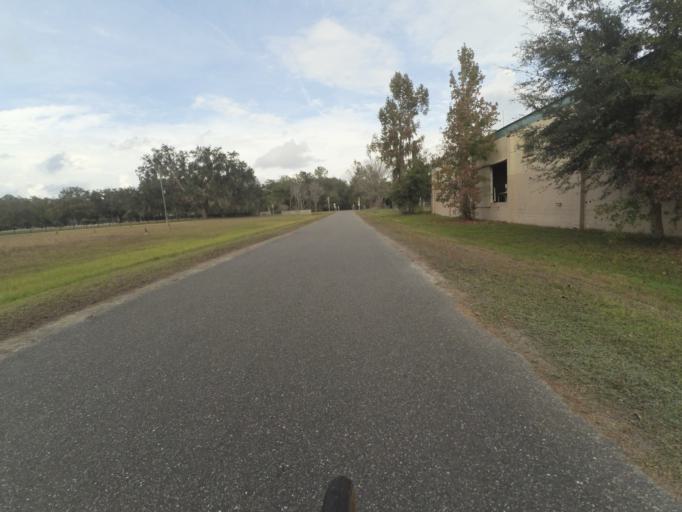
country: US
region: Florida
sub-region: Alachua County
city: Gainesville
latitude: 29.6309
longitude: -82.3122
